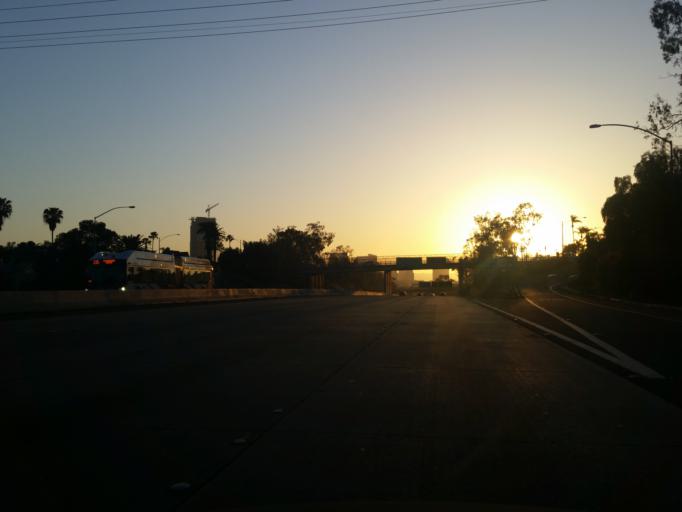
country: US
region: California
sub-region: San Diego County
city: San Diego
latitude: 32.7134
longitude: -117.1379
